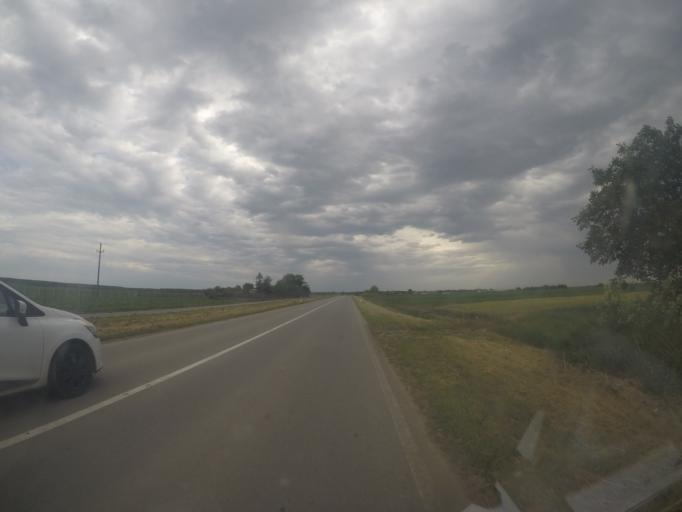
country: RS
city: Baranda
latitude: 45.0689
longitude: 20.4377
